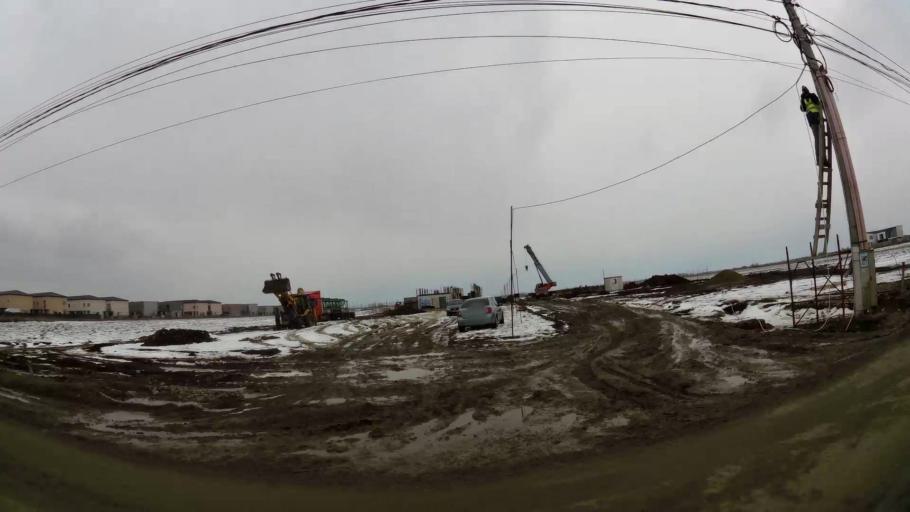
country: RO
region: Ilfov
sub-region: Comuna Tunari
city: Tunari
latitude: 44.5514
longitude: 26.1138
